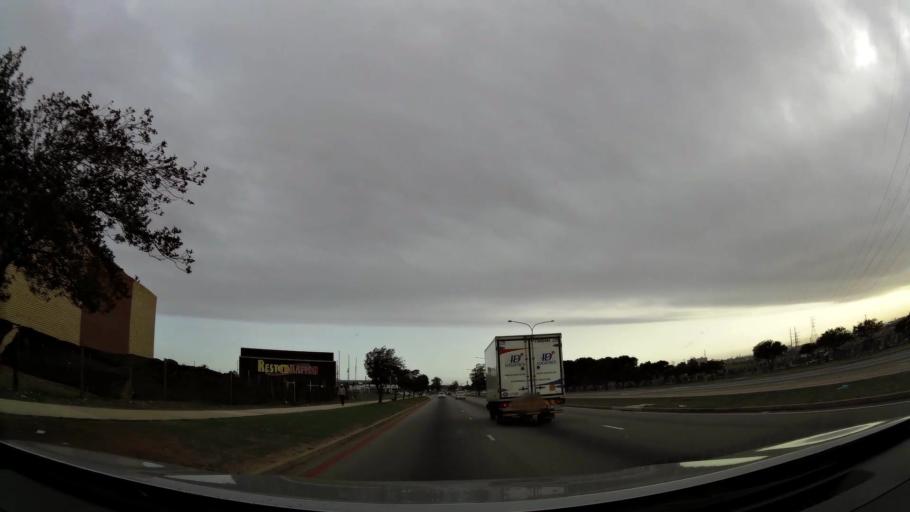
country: ZA
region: Eastern Cape
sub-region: Nelson Mandela Bay Metropolitan Municipality
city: Port Elizabeth
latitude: -33.9216
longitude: 25.5658
